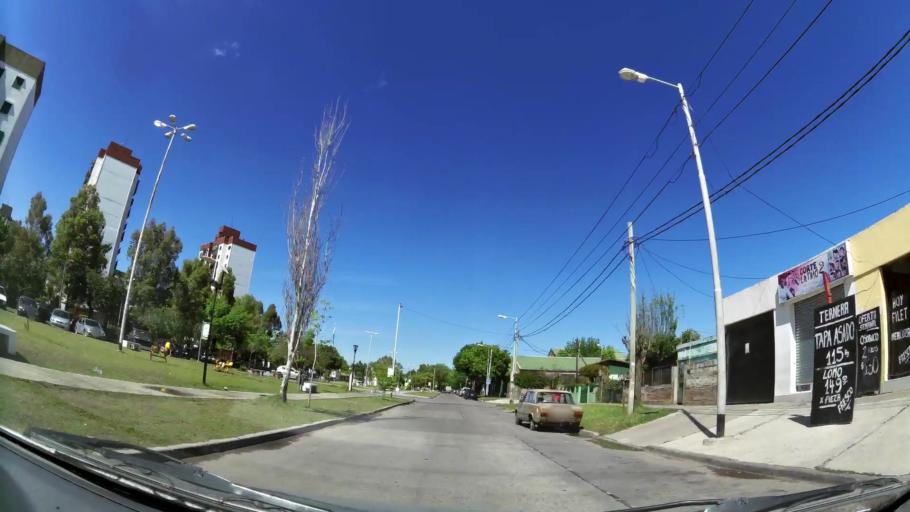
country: AR
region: Buenos Aires
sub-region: Partido de Quilmes
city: Quilmes
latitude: -34.6907
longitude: -58.3024
